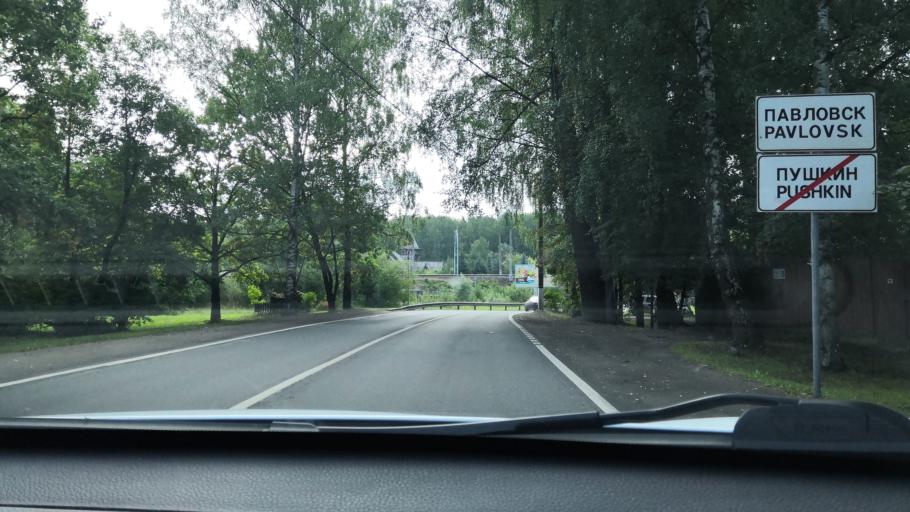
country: RU
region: St.-Petersburg
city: Pavlovsk
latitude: 59.6970
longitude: 30.4351
